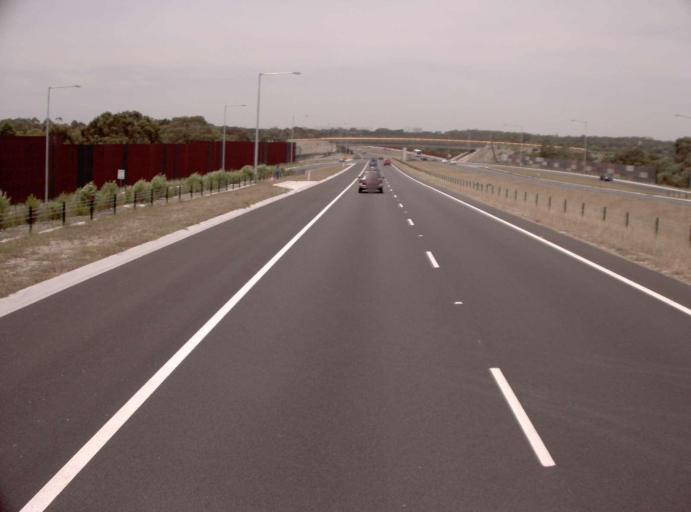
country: AU
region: Victoria
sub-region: Frankston
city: Carrum Downs
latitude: -38.1103
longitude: 145.1628
